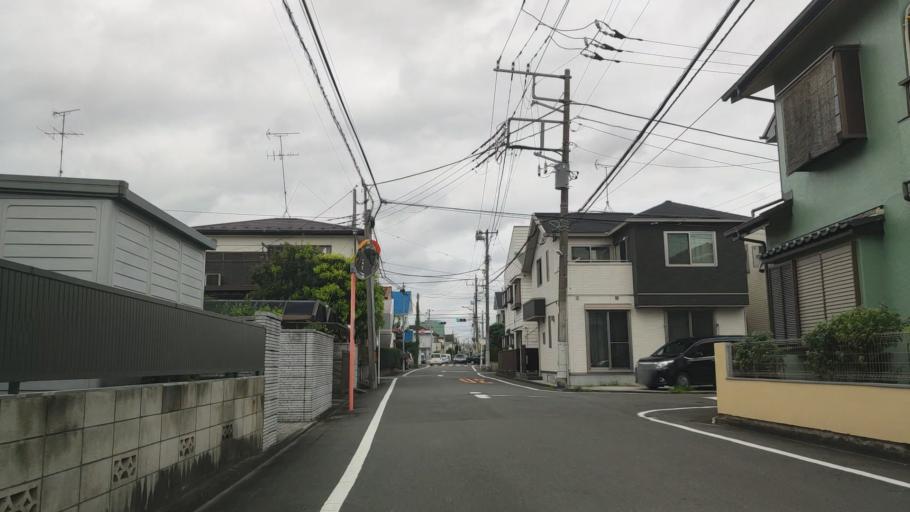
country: JP
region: Tokyo
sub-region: Machida-shi
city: Machida
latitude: 35.5143
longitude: 139.4365
